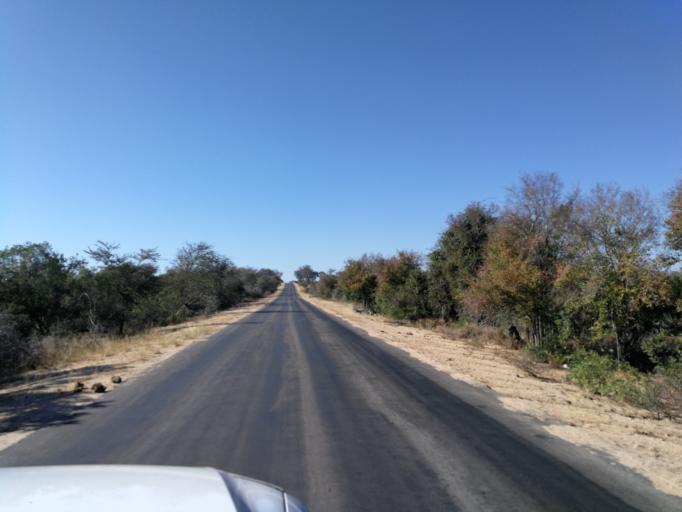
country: ZA
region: Limpopo
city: Thulamahashi
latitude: -24.9826
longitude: 31.4873
